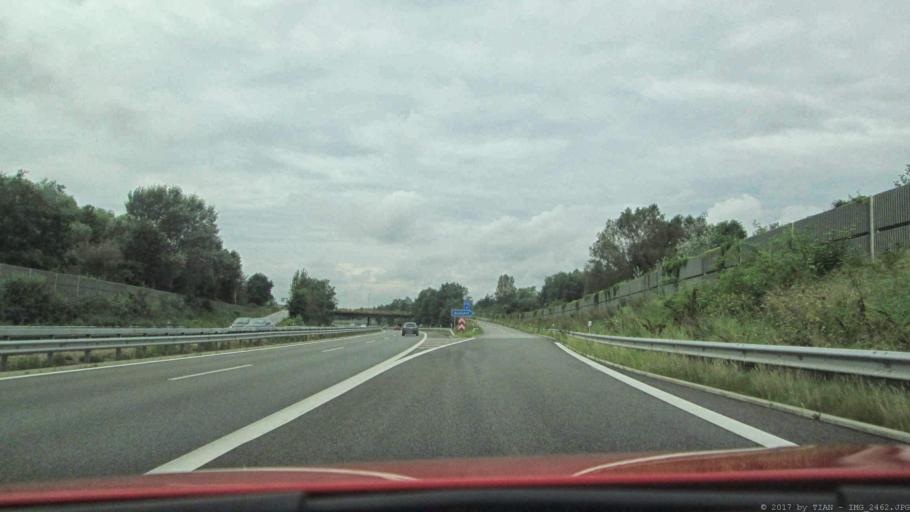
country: DE
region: Hamburg
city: Bergedorf
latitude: 53.4752
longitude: 10.2437
